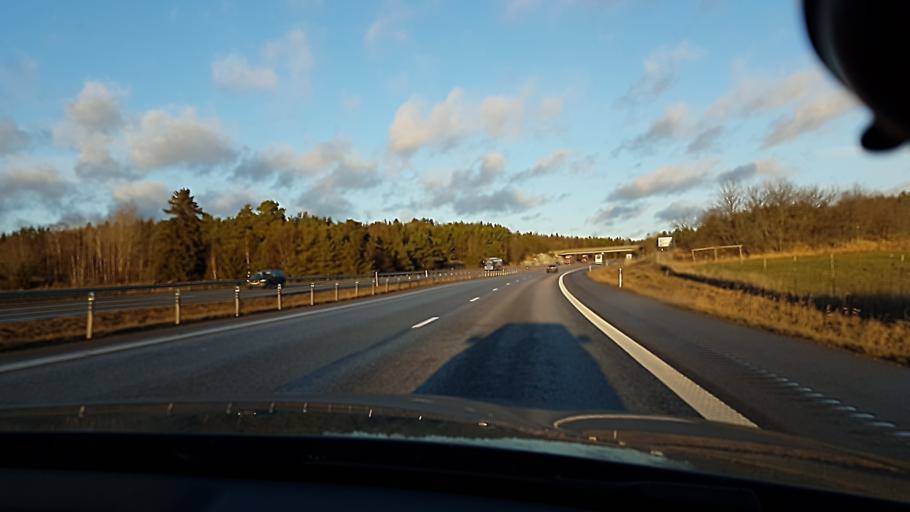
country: SE
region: Soedermanland
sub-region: Trosa Kommun
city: Vagnharad
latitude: 58.9516
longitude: 17.4370
